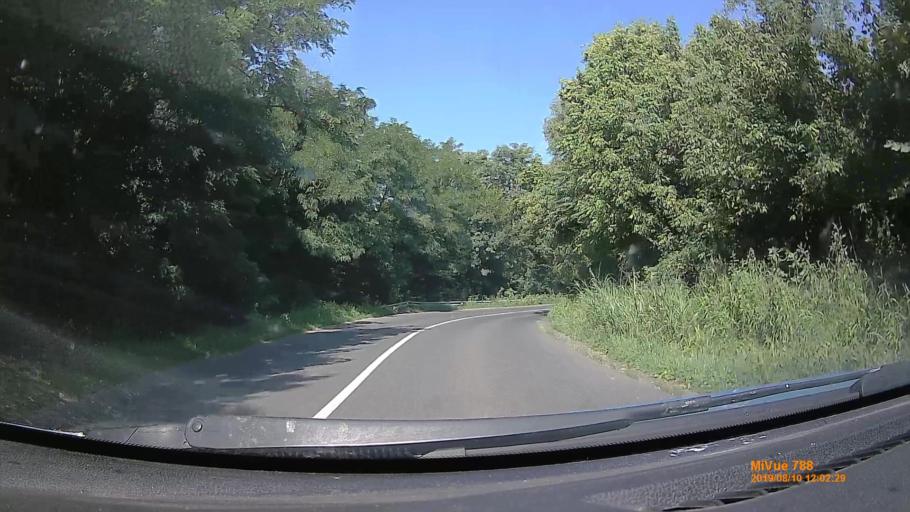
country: HU
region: Somogy
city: Somogyvar
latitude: 46.5738
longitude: 17.6482
